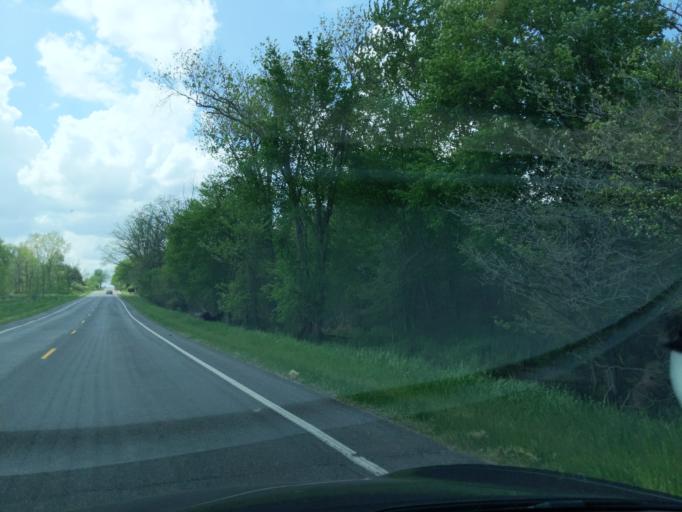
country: US
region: Michigan
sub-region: Ingham County
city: Mason
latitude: 42.5964
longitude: -84.4137
